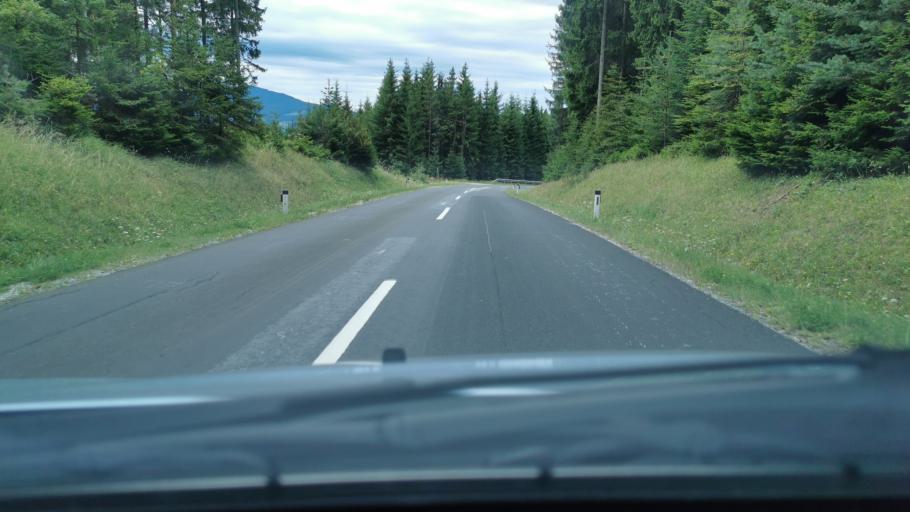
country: AT
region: Styria
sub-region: Politischer Bezirk Weiz
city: Fischbach
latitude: 47.4176
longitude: 15.6587
